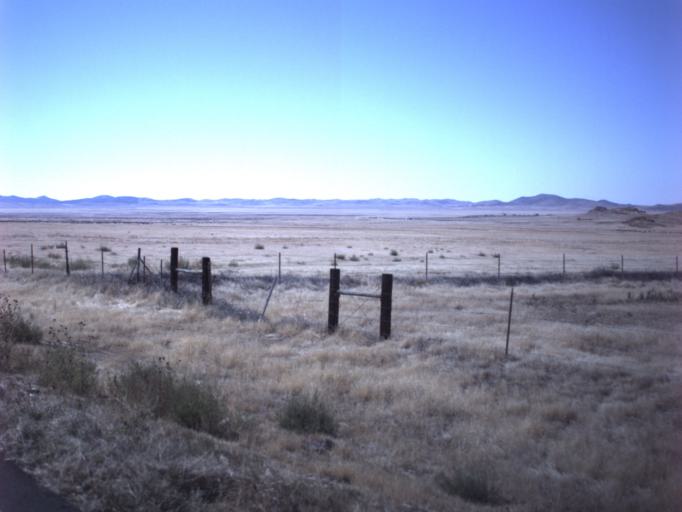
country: US
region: Utah
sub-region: Tooele County
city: Grantsville
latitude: 40.3904
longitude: -112.7474
